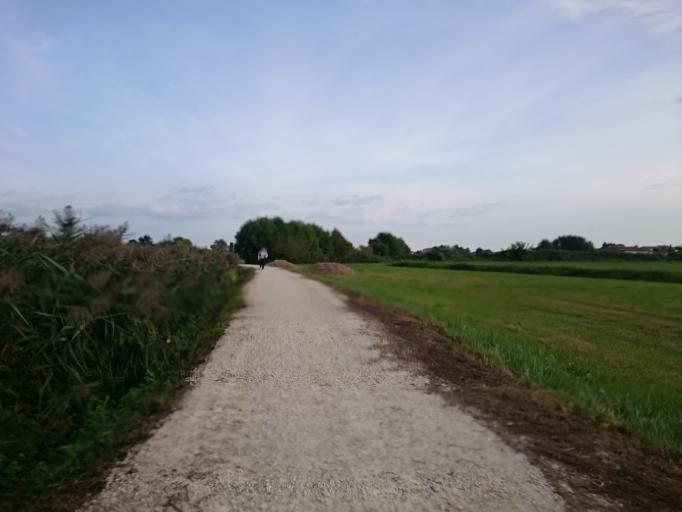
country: IT
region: Veneto
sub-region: Provincia di Vicenza
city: Camisano Vicentino
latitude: 45.5329
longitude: 11.6918
